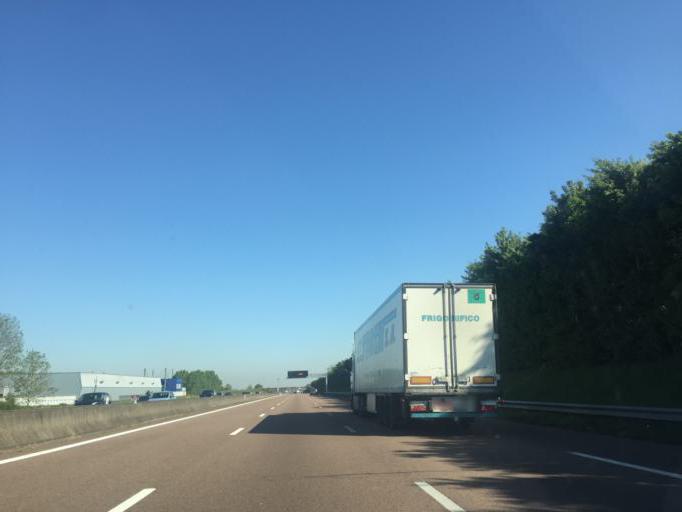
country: FR
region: Bourgogne
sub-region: Departement de Saone-et-Loire
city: Sevrey
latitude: 46.7279
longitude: 4.8371
